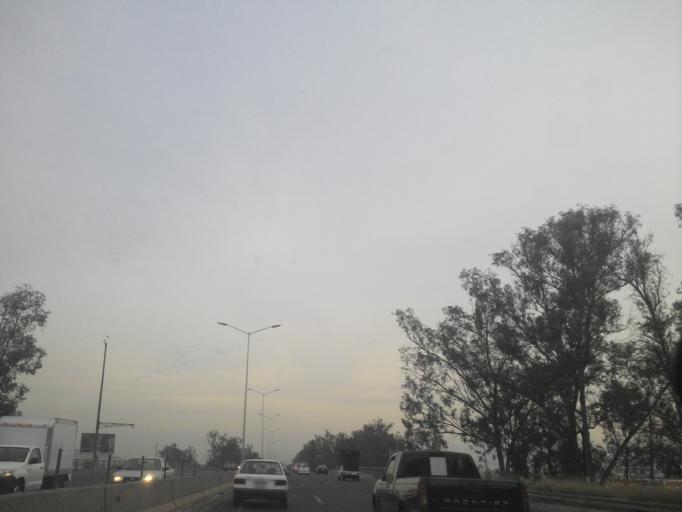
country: MX
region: Jalisco
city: Guadalajara
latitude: 20.6594
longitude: -103.4481
